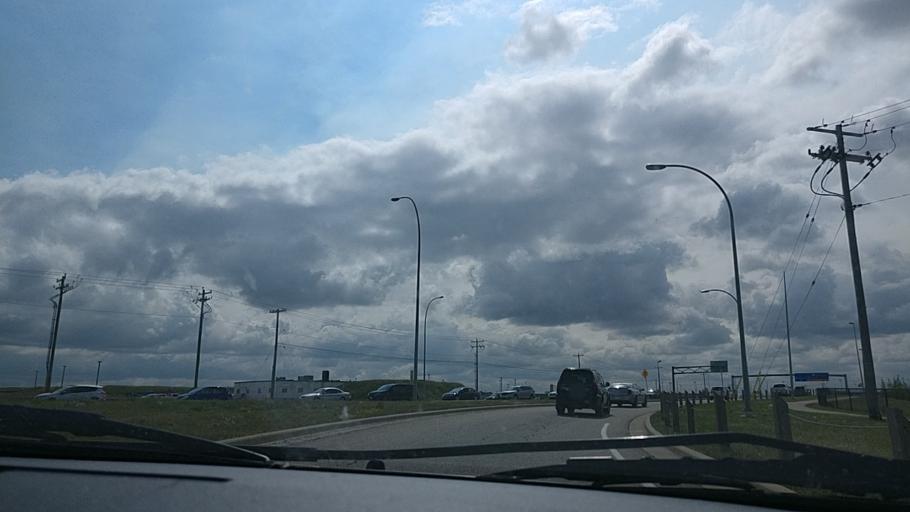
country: CA
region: Alberta
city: Calgary
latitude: 51.1390
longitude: -114.0026
